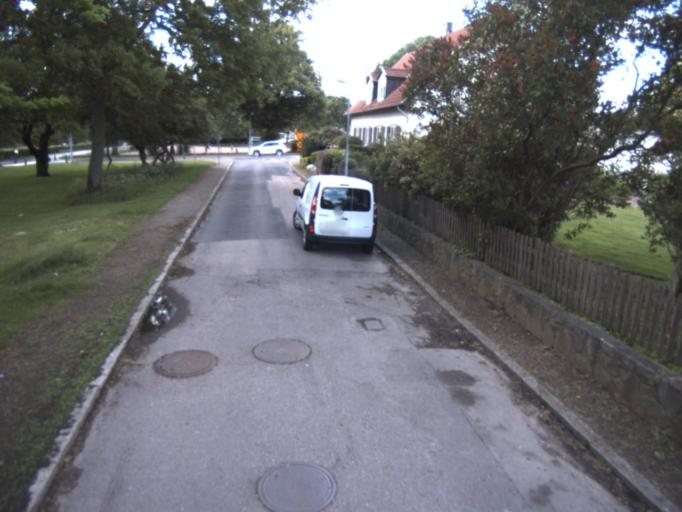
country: SE
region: Skane
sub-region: Helsingborg
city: Helsingborg
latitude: 56.0400
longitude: 12.7183
